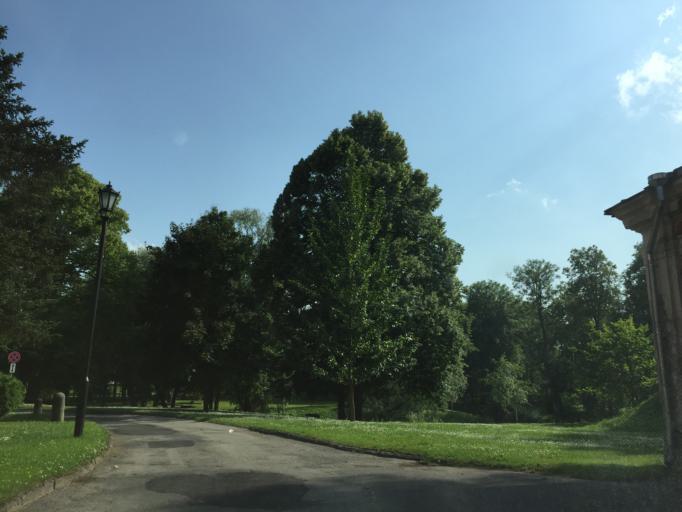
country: LV
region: Jelgava
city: Jelgava
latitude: 56.6559
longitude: 23.7313
